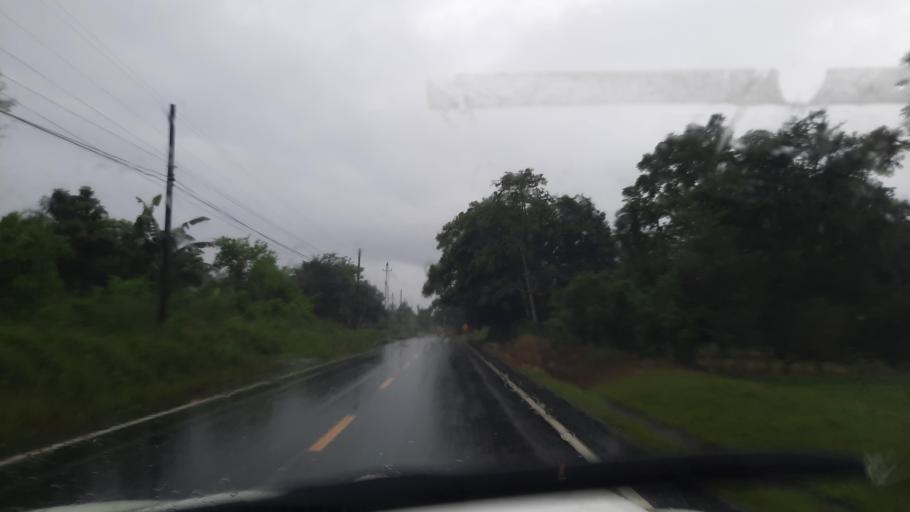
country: PA
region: Chiriqui
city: Sortova
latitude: 8.5813
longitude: -82.6372
